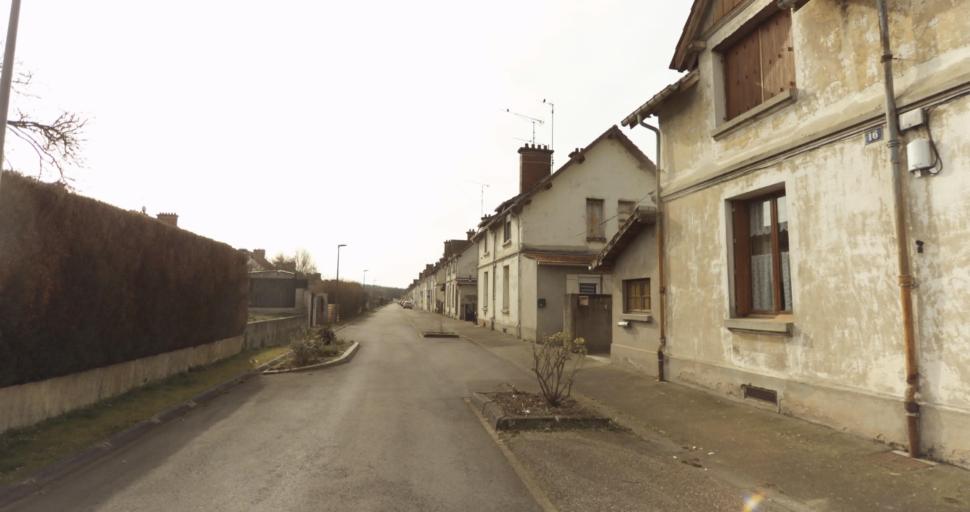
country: FR
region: Lorraine
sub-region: Departement de Meurthe-et-Moselle
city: Jarny
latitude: 49.1458
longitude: 5.8796
